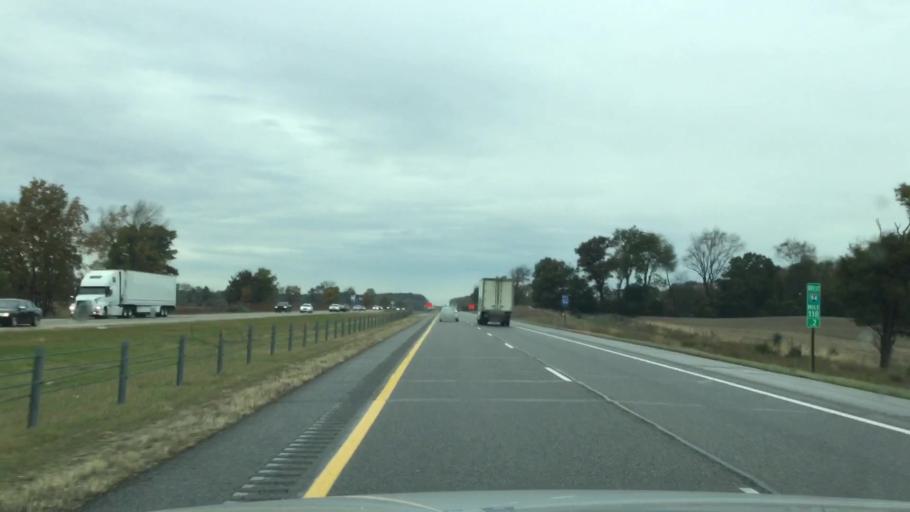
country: US
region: Michigan
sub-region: Calhoun County
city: Albion
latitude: 42.2838
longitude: -84.8078
